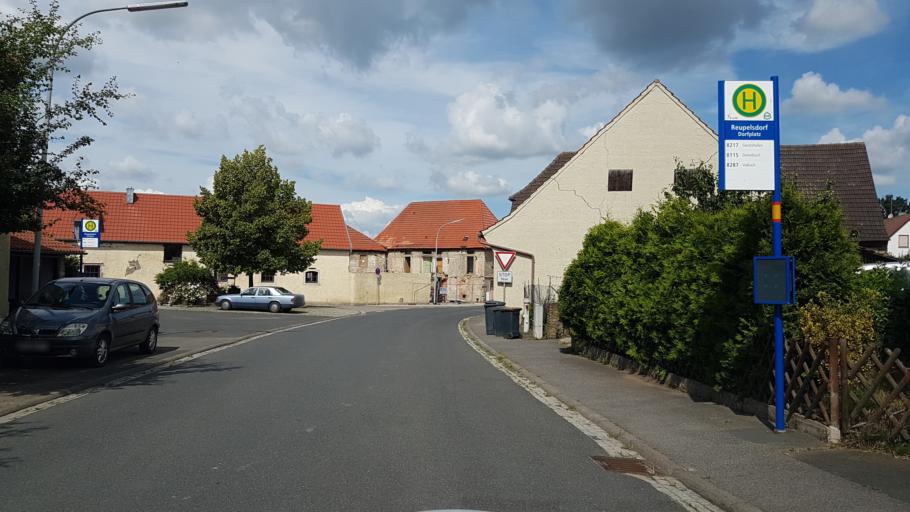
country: DE
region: Bavaria
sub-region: Regierungsbezirk Unterfranken
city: Kleinlangheim
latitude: 49.8125
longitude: 10.2913
